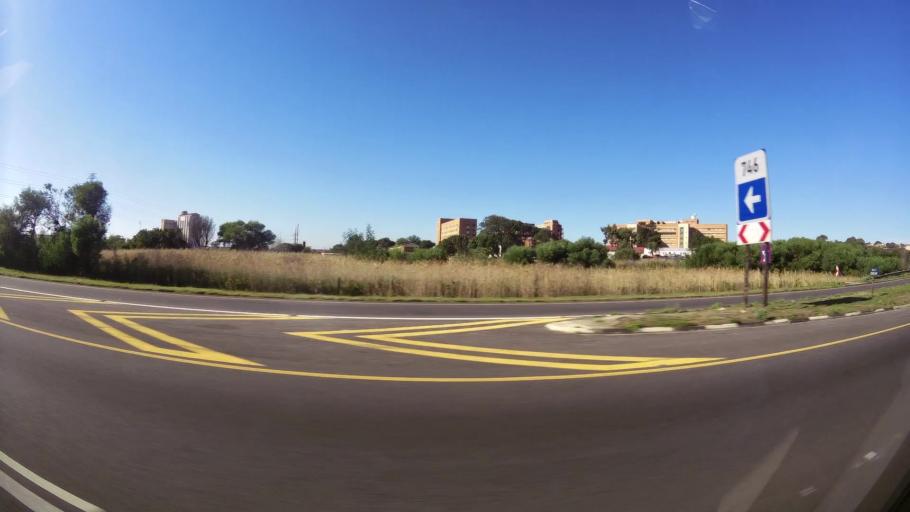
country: ZA
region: Eastern Cape
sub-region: Nelson Mandela Bay Metropolitan Municipality
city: Port Elizabeth
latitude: -33.9221
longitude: 25.5687
